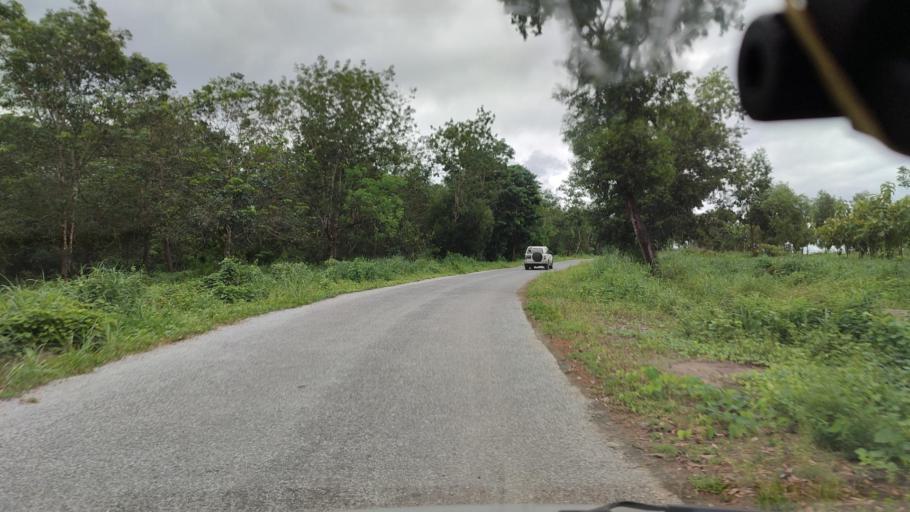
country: MM
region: Bago
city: Thanatpin
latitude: 17.2466
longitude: 96.3261
